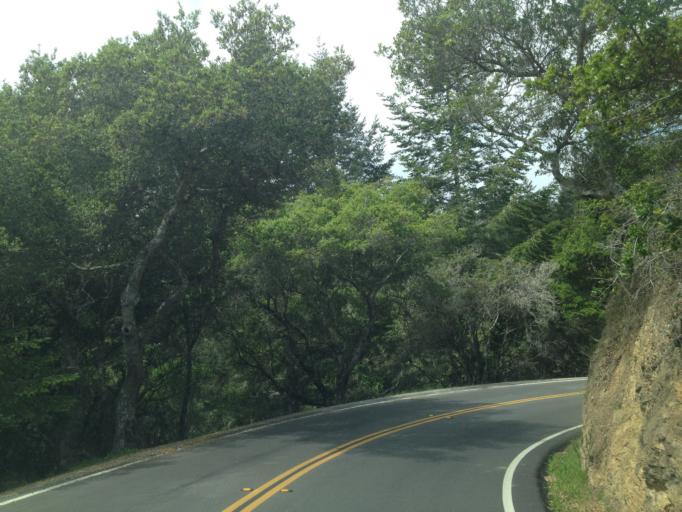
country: US
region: California
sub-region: Marin County
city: Tamalpais Valley
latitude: 37.8931
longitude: -122.5666
